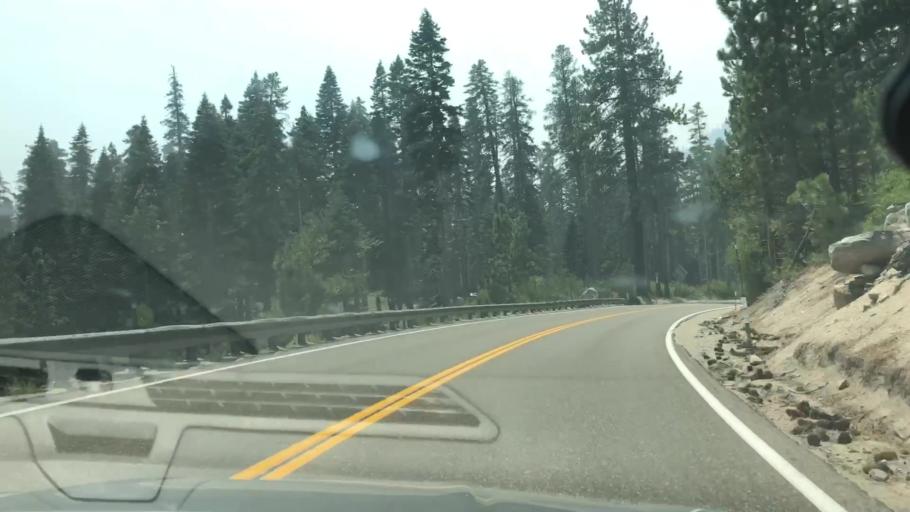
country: US
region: California
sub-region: El Dorado County
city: South Lake Tahoe
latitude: 38.8139
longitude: -120.0286
